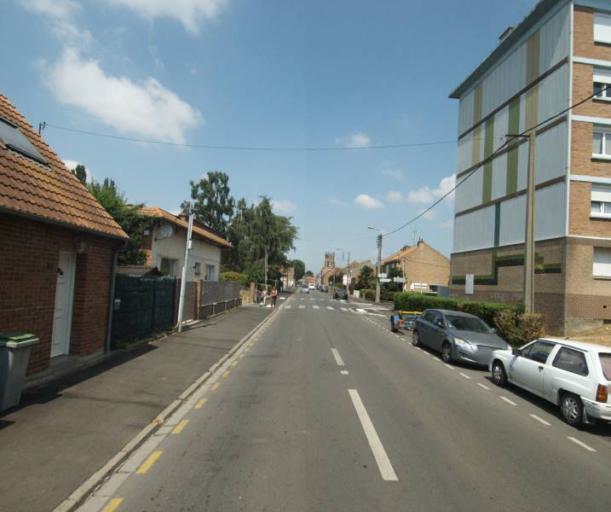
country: FR
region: Nord-Pas-de-Calais
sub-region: Departement du Nord
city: Armentieres
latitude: 50.6974
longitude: 2.8838
